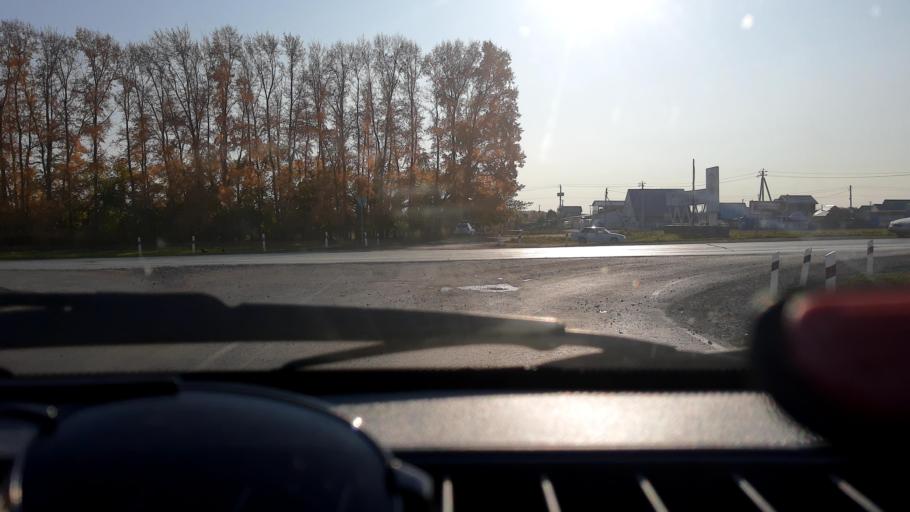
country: RU
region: Bashkortostan
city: Kabakovo
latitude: 54.4689
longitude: 55.9499
